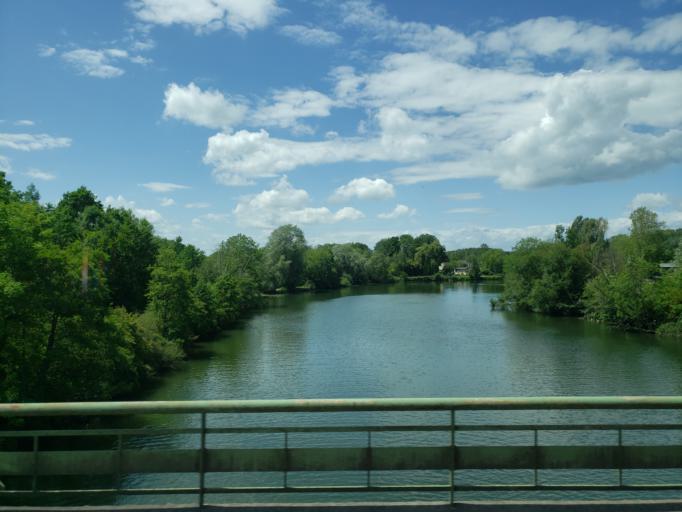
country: FR
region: Bourgogne
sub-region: Departement de l'Yonne
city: Migennes
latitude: 47.9545
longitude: 3.5047
